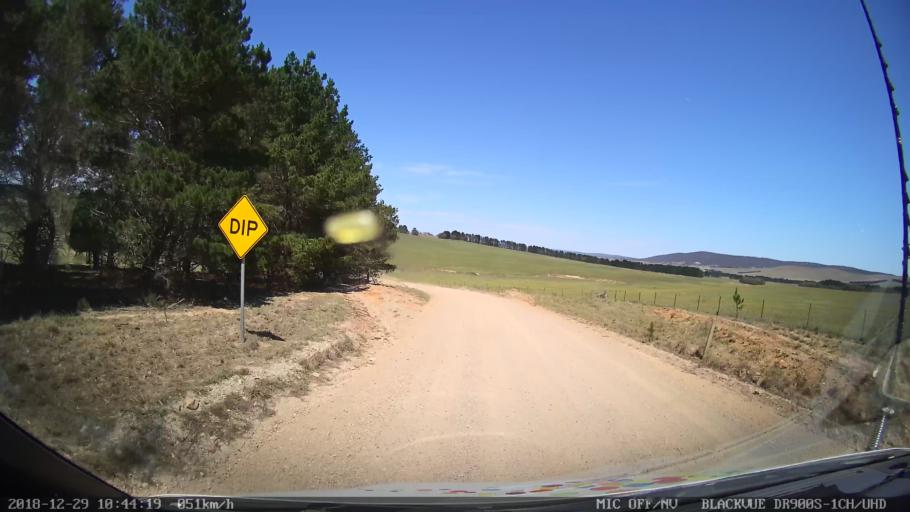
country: AU
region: New South Wales
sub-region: Palerang
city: Bungendore
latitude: -35.0415
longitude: 149.5294
